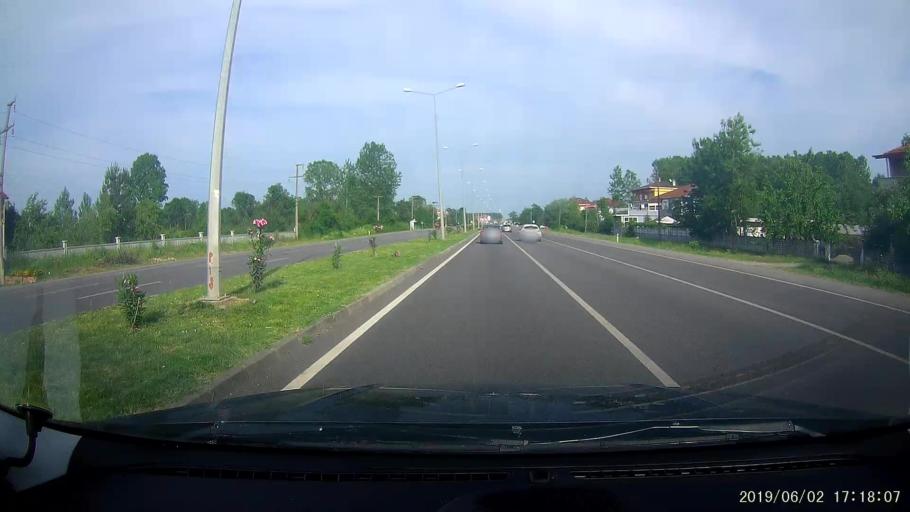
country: TR
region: Samsun
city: Dikbiyik
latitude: 41.2252
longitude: 36.5927
